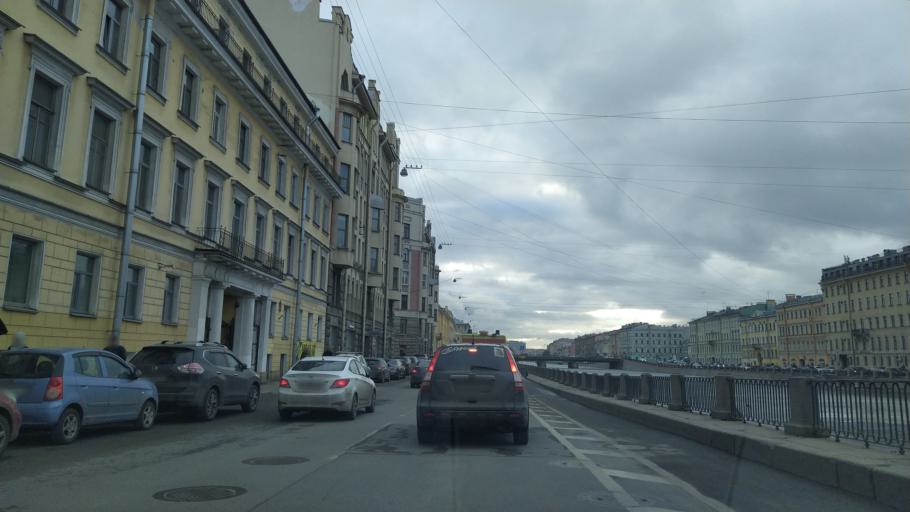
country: RU
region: St.-Petersburg
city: Saint Petersburg
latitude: 59.9266
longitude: 30.3318
